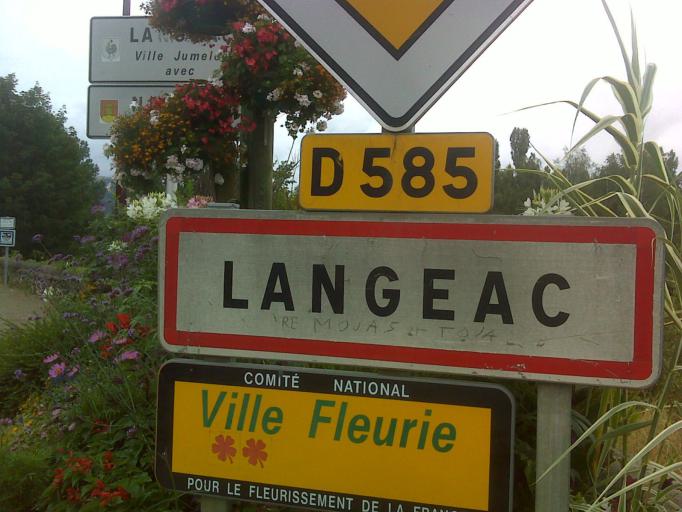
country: FR
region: Auvergne
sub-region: Departement de la Haute-Loire
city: Langeac
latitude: 45.0932
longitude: 3.5039
